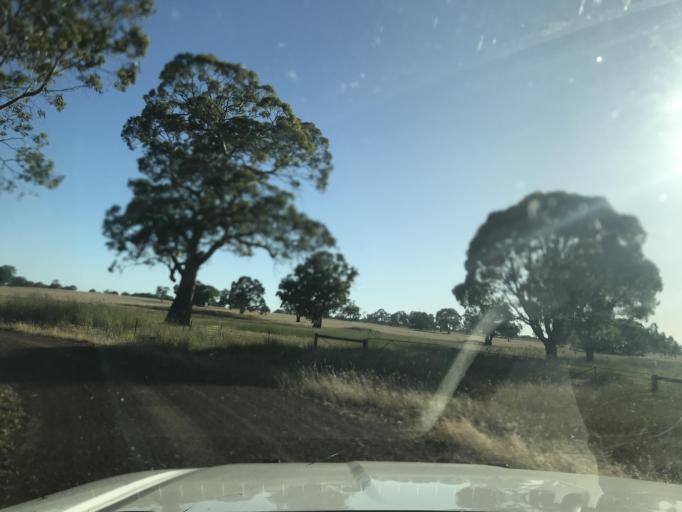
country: AU
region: South Australia
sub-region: Wattle Range
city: Penola
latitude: -37.0356
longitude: 141.3719
